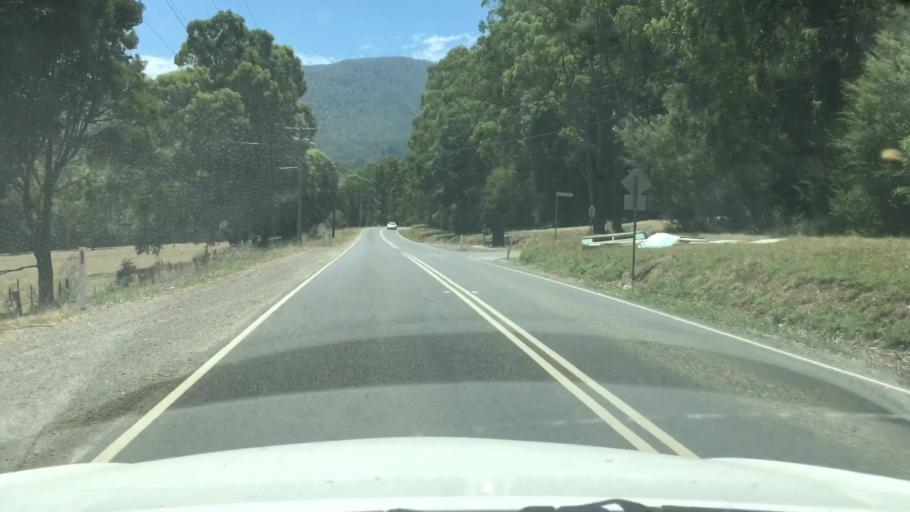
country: AU
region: Victoria
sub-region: Yarra Ranges
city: Millgrove
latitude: -37.7294
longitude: 145.7492
